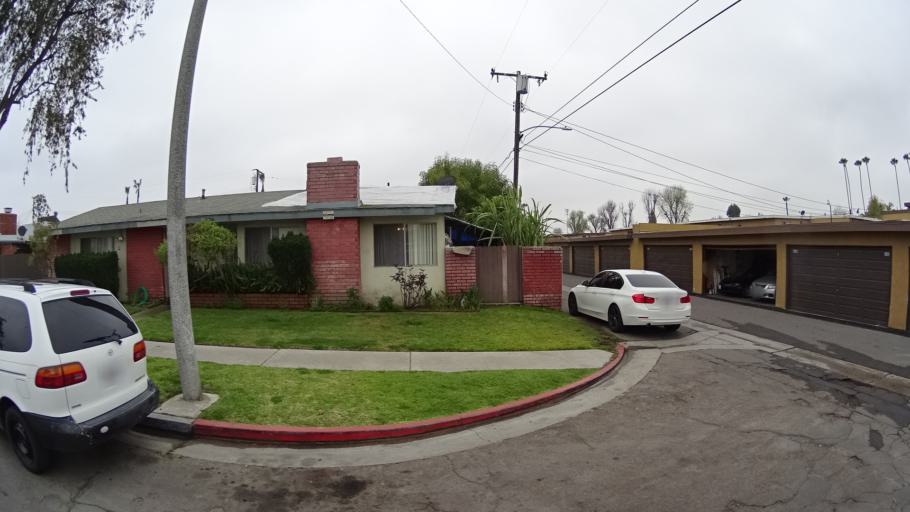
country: US
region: California
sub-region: Orange County
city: Stanton
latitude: 33.8306
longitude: -118.0044
